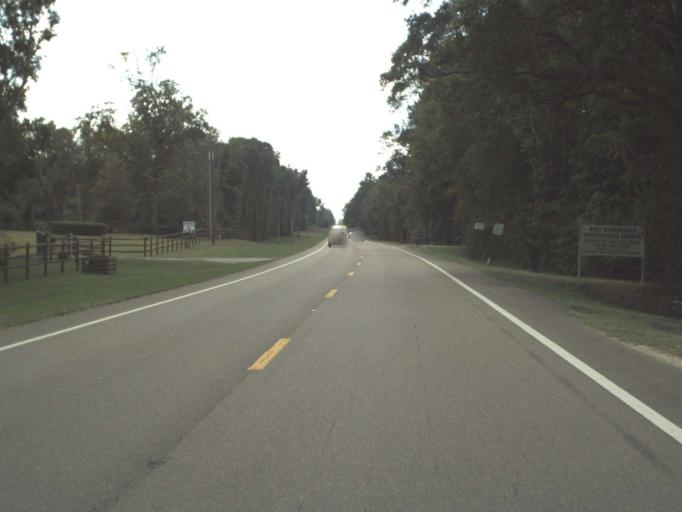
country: US
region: Florida
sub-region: Walton County
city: DeFuniak Springs
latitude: 30.6958
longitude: -85.9364
